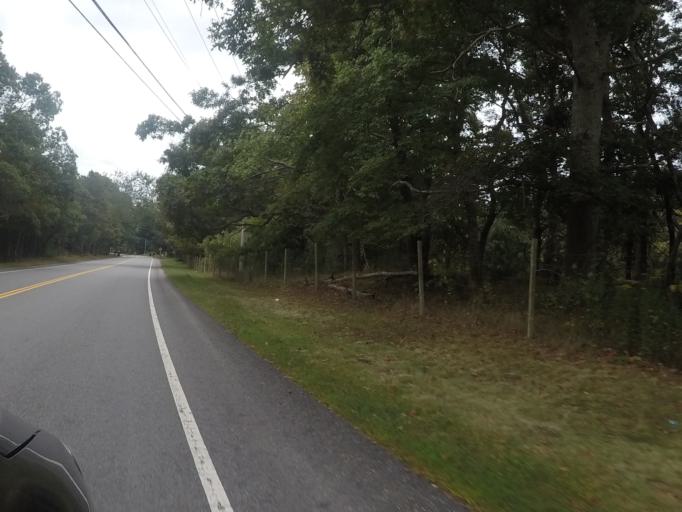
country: US
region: Massachusetts
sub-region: Bristol County
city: Smith Mills
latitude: 41.5878
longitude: -71.0007
